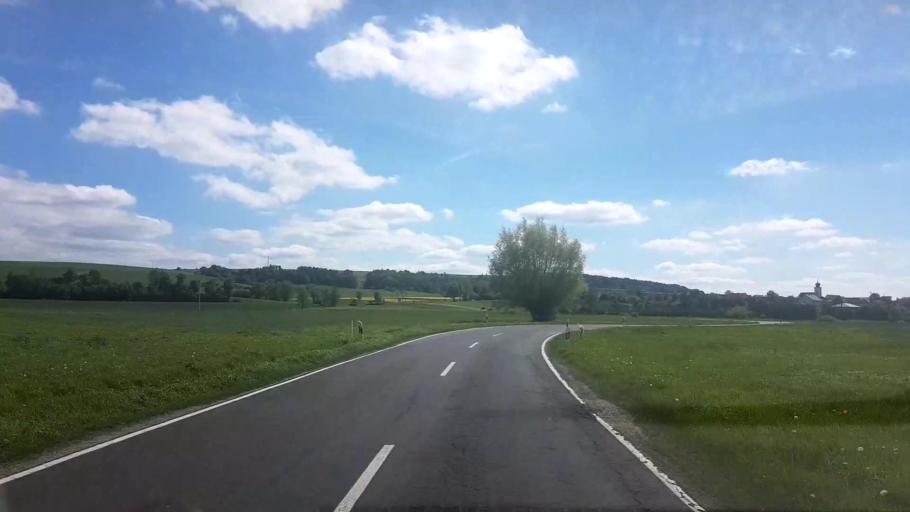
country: DE
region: Bavaria
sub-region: Regierungsbezirk Unterfranken
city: Untermerzbach
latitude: 50.1310
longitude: 10.8856
